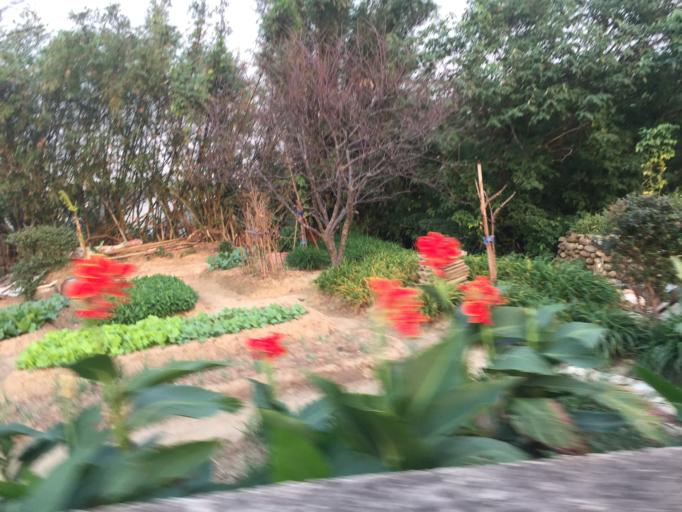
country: TW
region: Taiwan
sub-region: Miaoli
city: Miaoli
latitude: 24.4906
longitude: 120.7768
